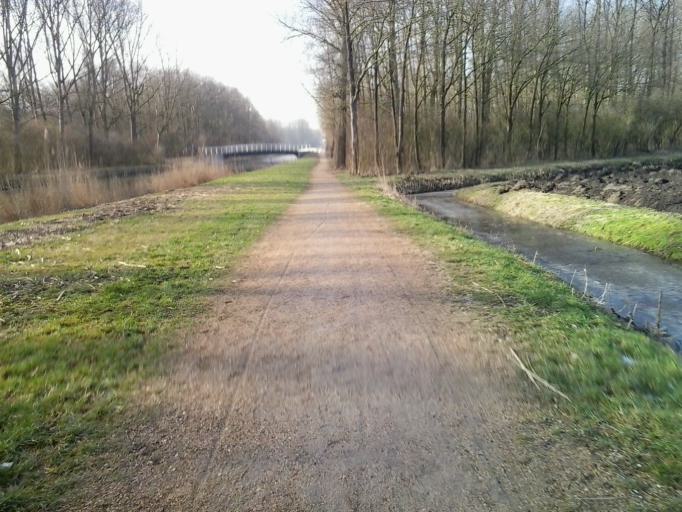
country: NL
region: South Holland
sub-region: Gemeente Lansingerland
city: Bergschenhoek
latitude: 51.9744
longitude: 4.5142
